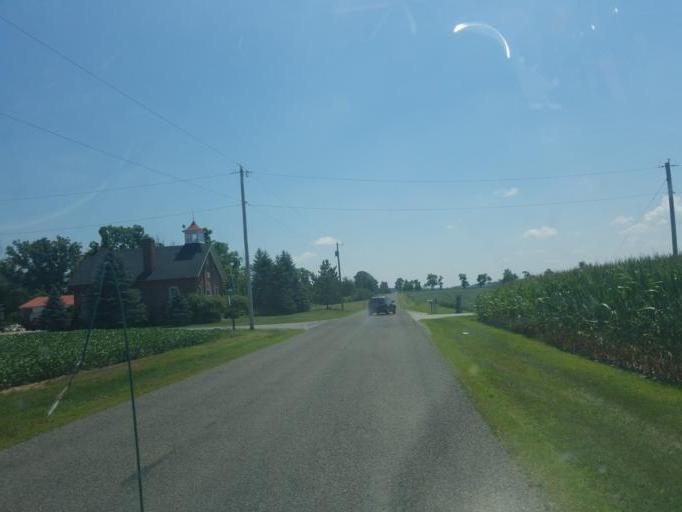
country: US
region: Ohio
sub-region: Auglaize County
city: Wapakoneta
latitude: 40.5335
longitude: -84.2311
